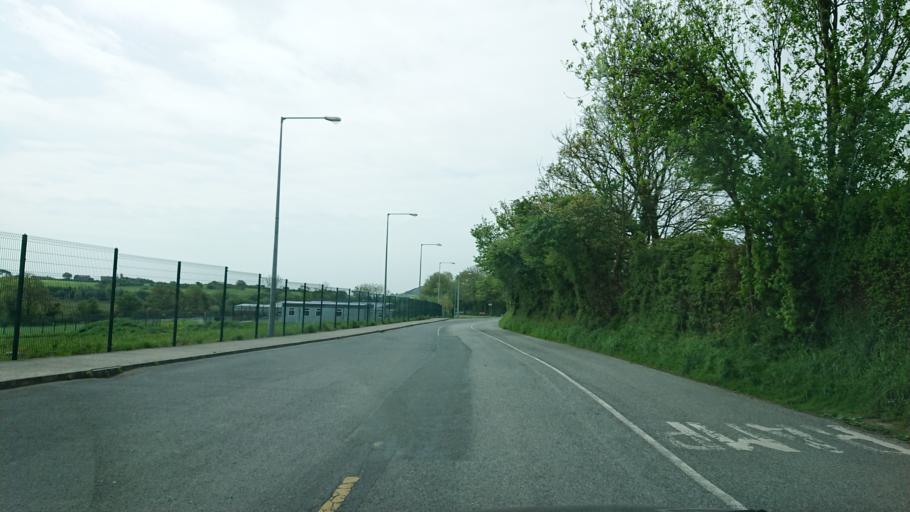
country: IE
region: Munster
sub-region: Waterford
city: Waterford
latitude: 52.2252
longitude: -7.0648
